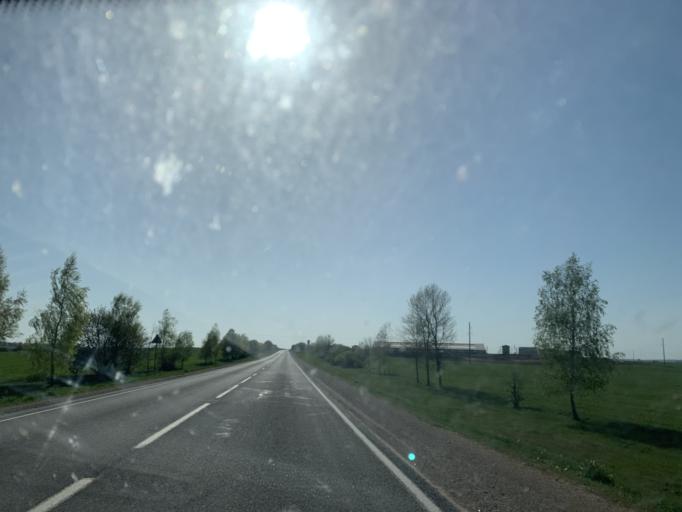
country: BY
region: Minsk
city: Kapyl'
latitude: 53.2545
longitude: 26.9218
